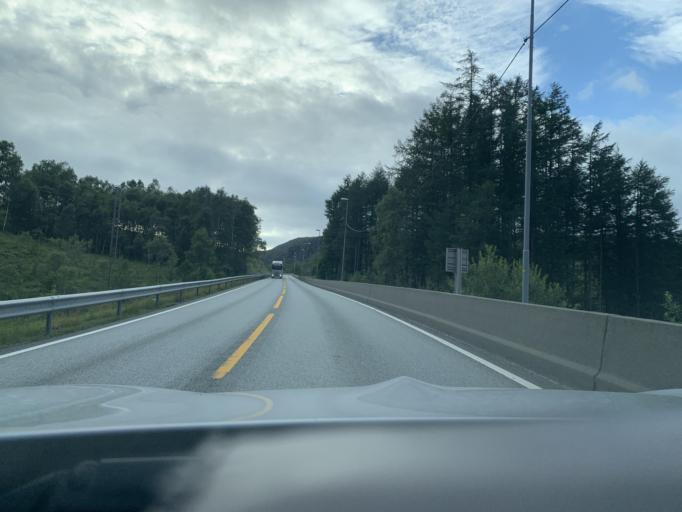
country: NO
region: Rogaland
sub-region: Bjerkreim
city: Vikesa
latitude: 58.6403
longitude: 6.0818
